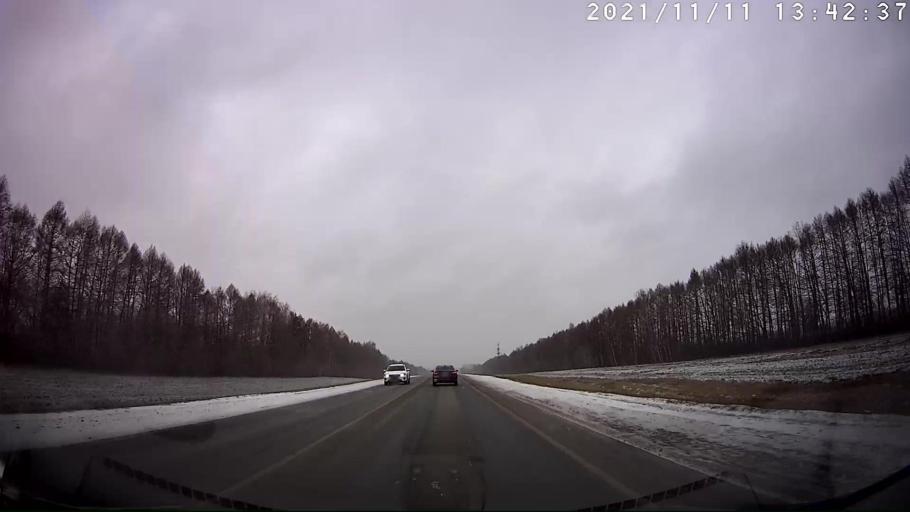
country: RU
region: Chuvashia
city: Kanash
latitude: 55.4779
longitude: 47.4830
